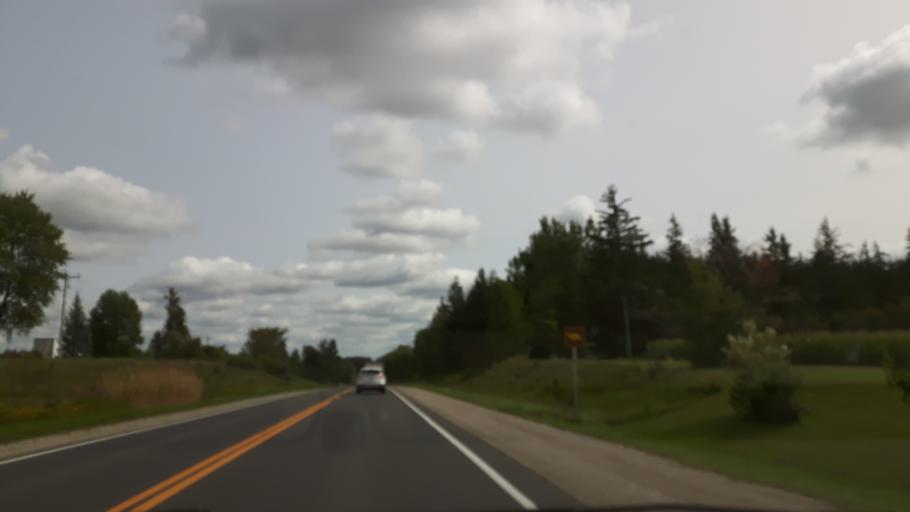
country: CA
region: Ontario
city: Bluewater
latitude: 43.6088
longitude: -81.5206
